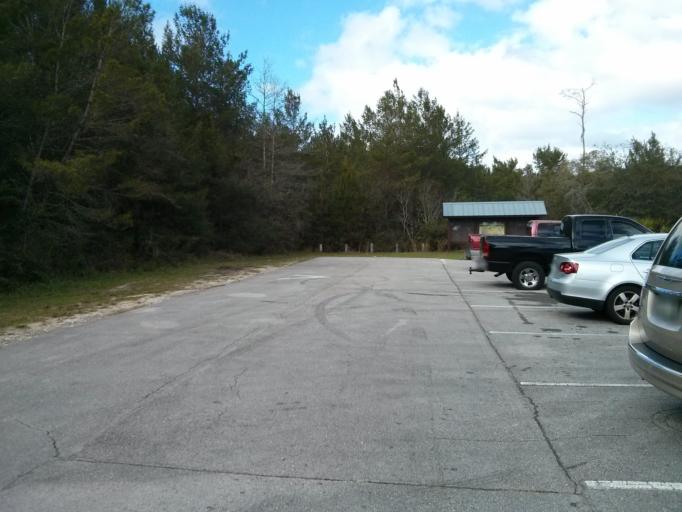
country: US
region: Florida
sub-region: Lake County
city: Astor
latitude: 29.0739
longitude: -81.6296
